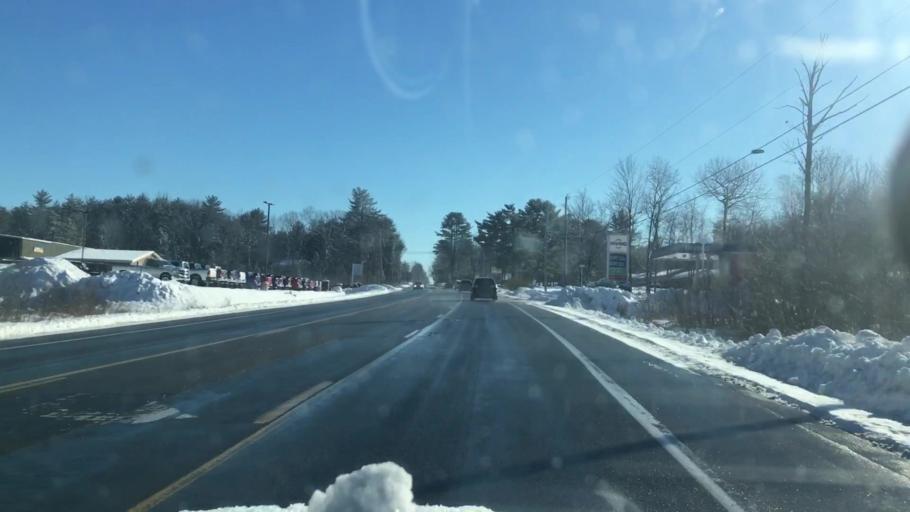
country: US
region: Maine
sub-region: Cumberland County
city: Bridgton
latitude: 44.0256
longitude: -70.6916
